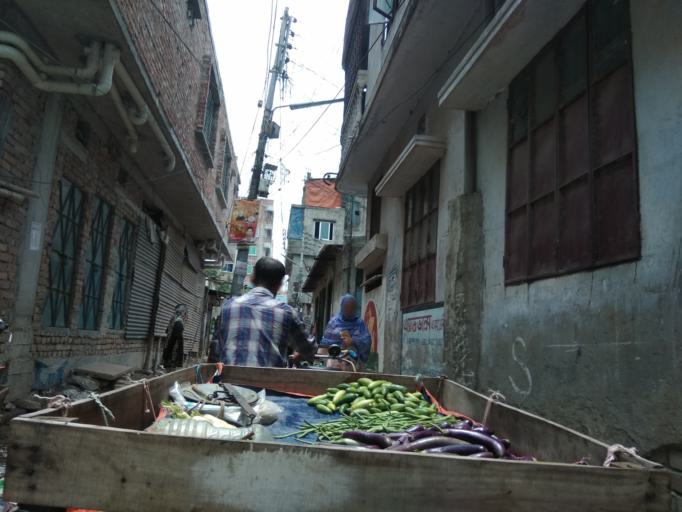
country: BD
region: Dhaka
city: Tungi
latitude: 23.8289
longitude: 90.3745
